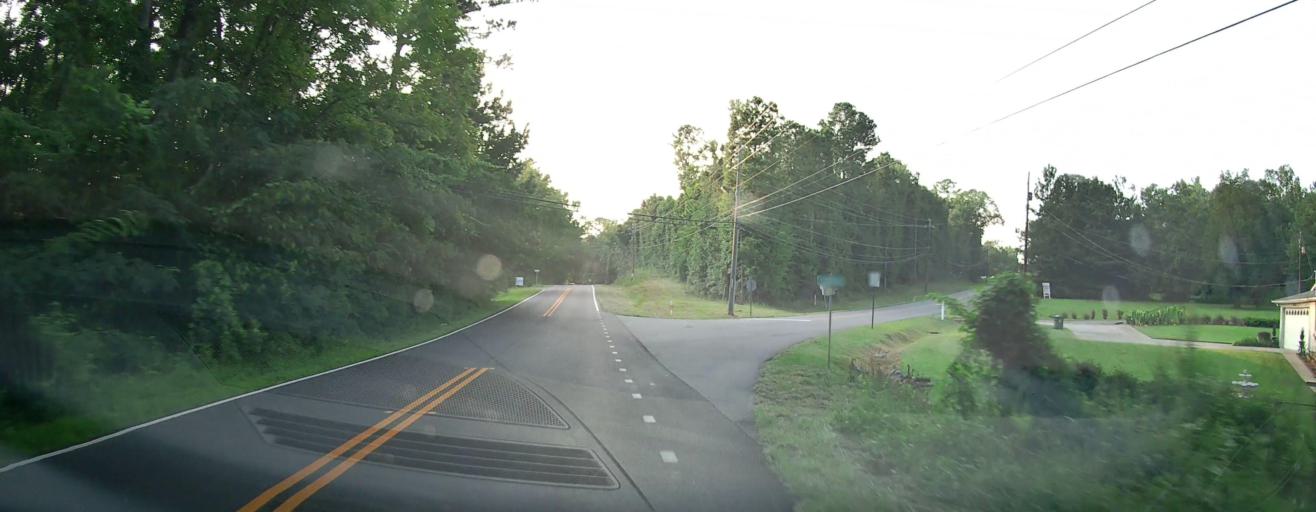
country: US
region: Georgia
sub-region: Bibb County
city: Macon
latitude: 32.9059
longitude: -83.7073
